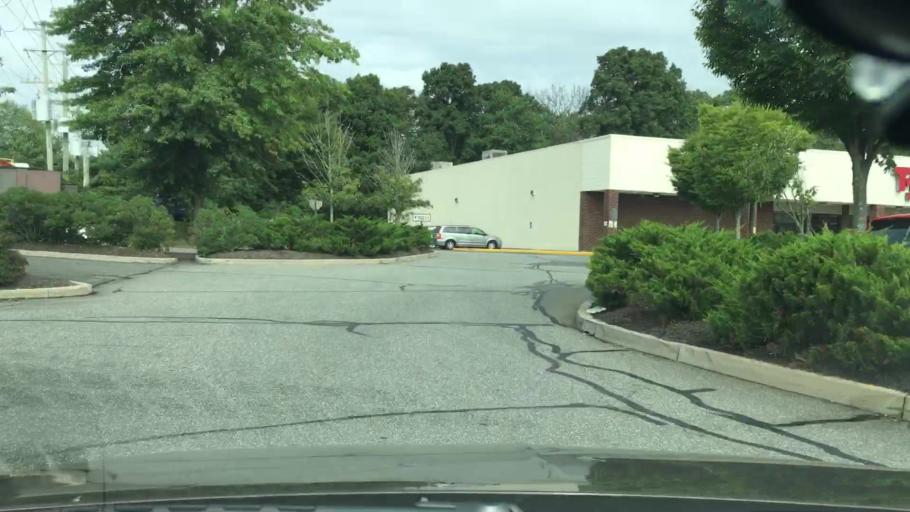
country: US
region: Connecticut
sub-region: Middlesex County
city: Clinton
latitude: 41.2732
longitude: -72.5063
